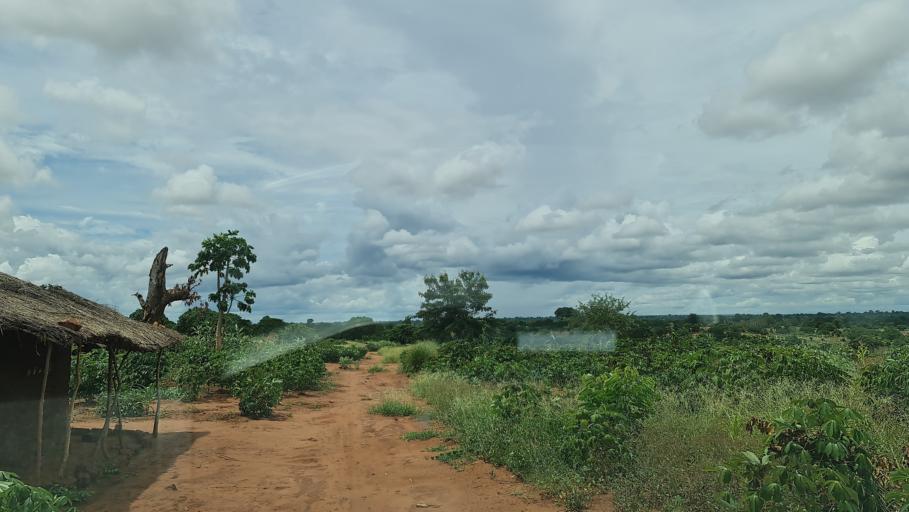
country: MZ
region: Nampula
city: Nacala
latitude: -14.7849
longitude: 39.9804
